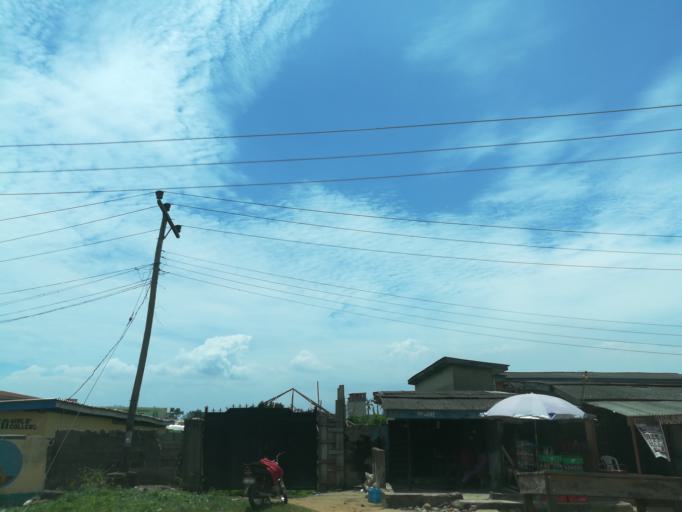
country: NG
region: Lagos
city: Ebute Ikorodu
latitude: 6.5968
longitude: 3.4935
